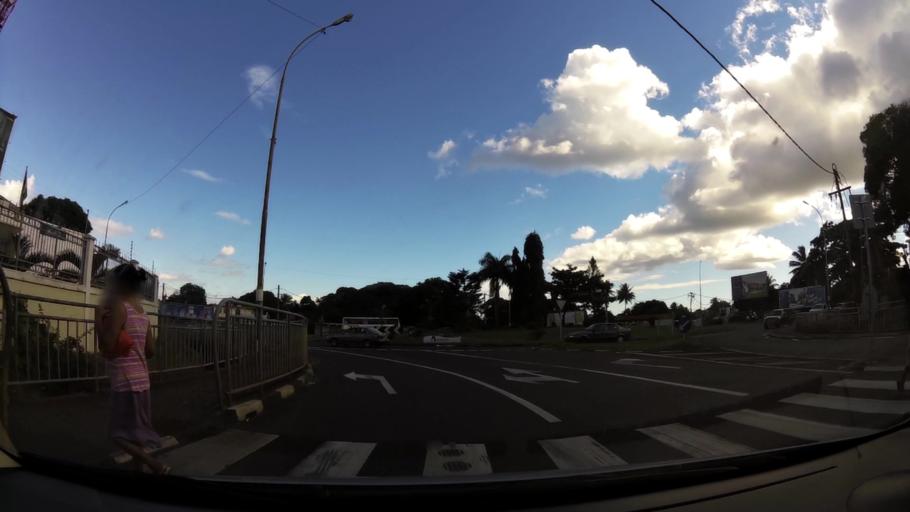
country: MU
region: Pamplemousses
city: Terre Rouge
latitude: -20.1267
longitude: 57.5323
